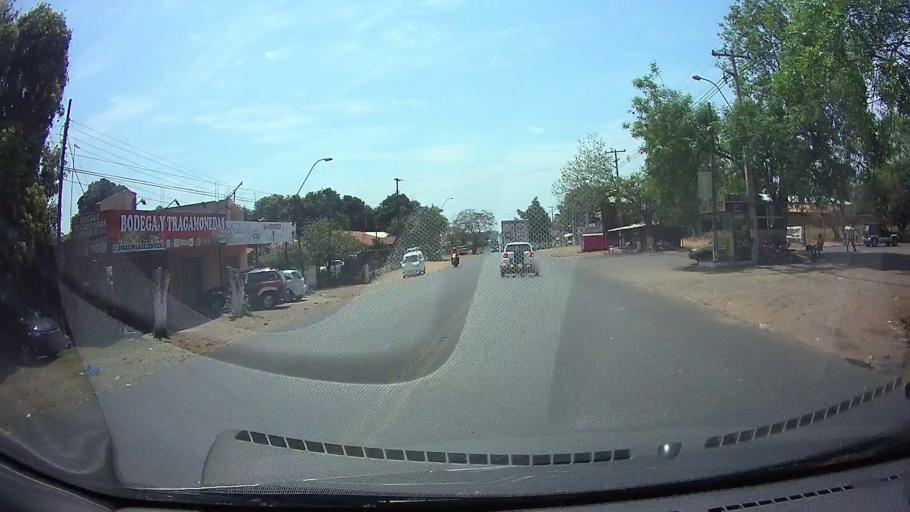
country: PY
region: Central
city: Capiata
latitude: -25.3999
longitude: -57.4649
